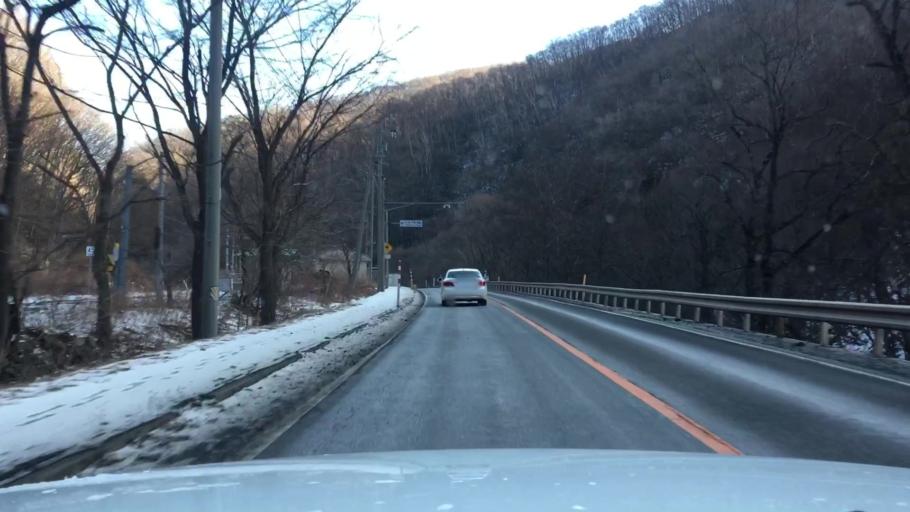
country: JP
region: Iwate
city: Tono
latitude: 39.6229
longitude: 141.5108
